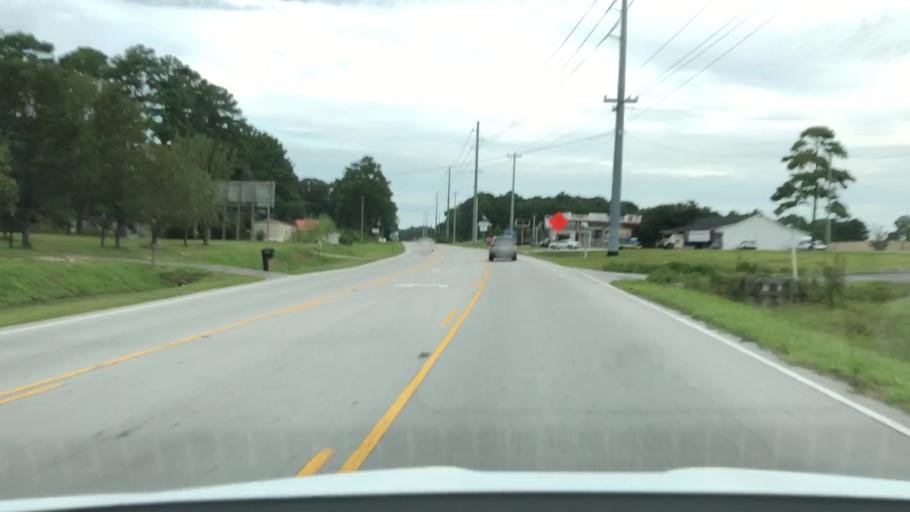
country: US
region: North Carolina
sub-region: Carteret County
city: Cape Carteret
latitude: 34.7152
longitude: -77.0683
